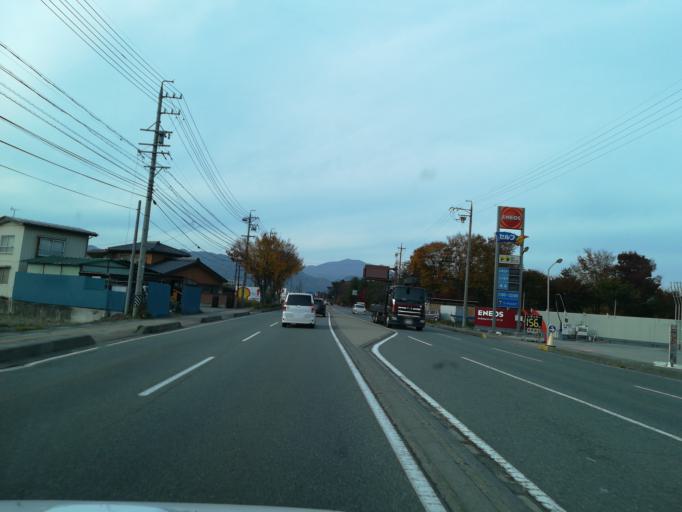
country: JP
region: Nagano
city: Nagano-shi
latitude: 36.5863
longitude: 138.1880
